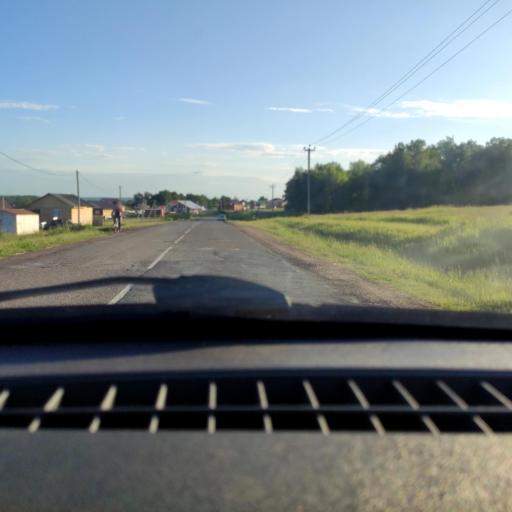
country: RU
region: Bashkortostan
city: Avdon
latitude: 54.6207
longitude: 55.6739
